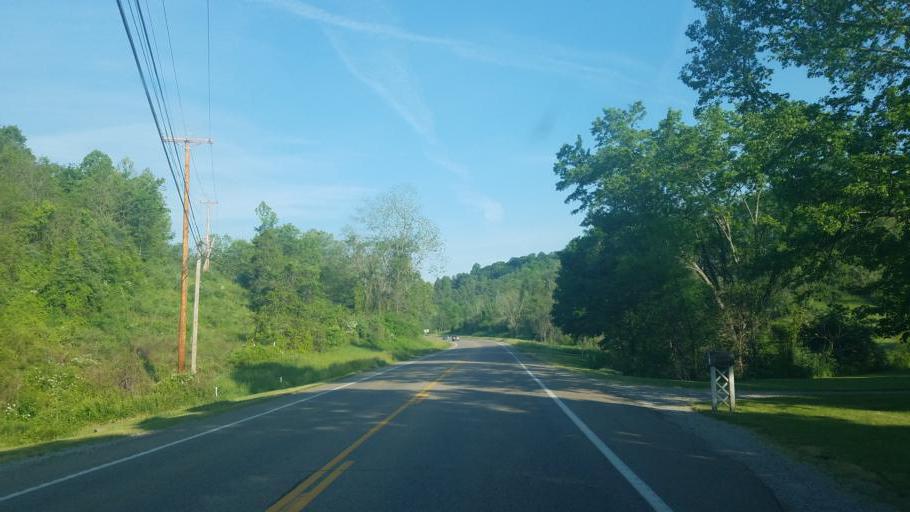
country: US
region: West Virginia
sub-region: Mason County
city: New Haven
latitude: 39.1160
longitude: -81.9025
